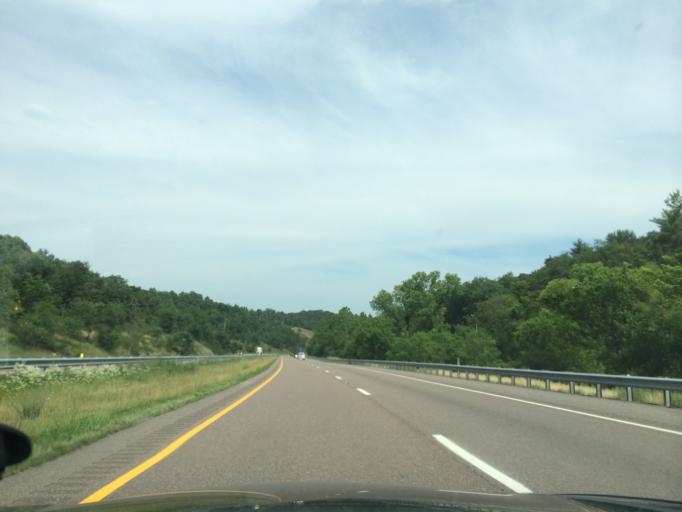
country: US
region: West Virginia
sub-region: Morgan County
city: Berkeley Springs
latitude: 39.6815
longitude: -78.4891
